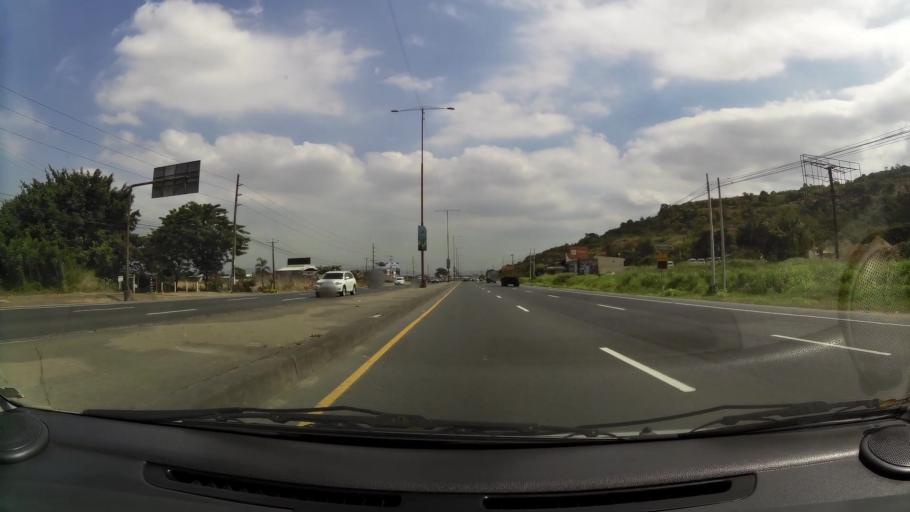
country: EC
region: Guayas
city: El Triunfo
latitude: -2.0546
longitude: -79.9178
